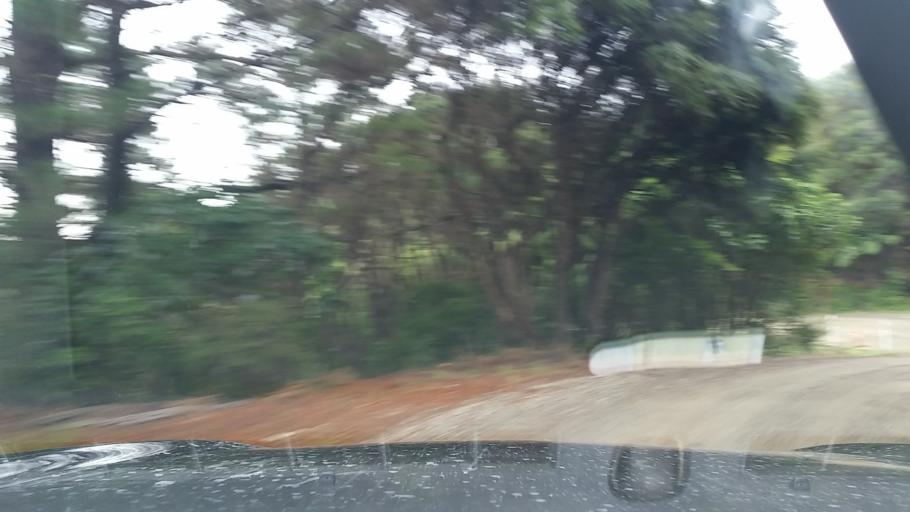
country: NZ
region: Marlborough
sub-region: Marlborough District
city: Picton
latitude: -41.1673
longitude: 174.0092
